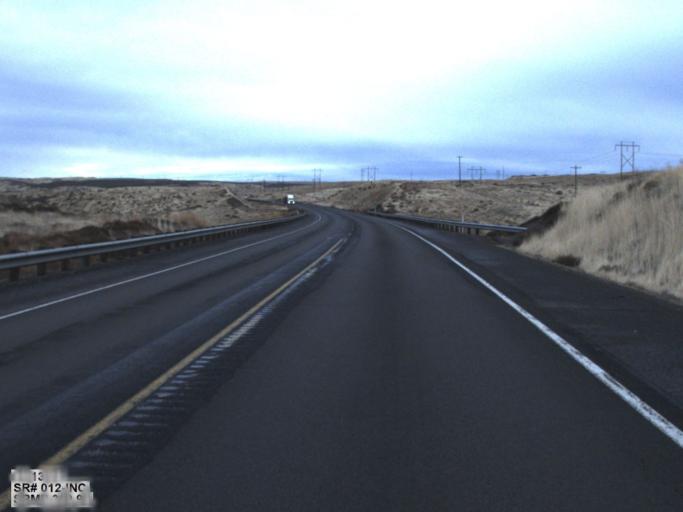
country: US
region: Washington
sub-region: Benton County
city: Finley
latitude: 46.0550
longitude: -118.8614
